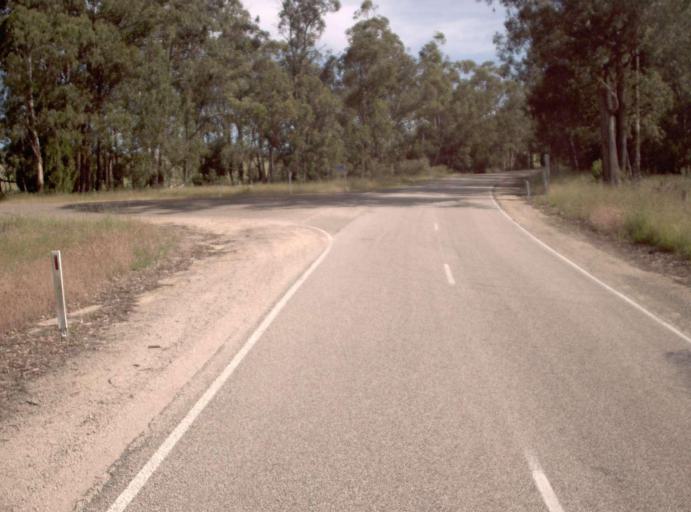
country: AU
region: Victoria
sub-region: East Gippsland
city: Lakes Entrance
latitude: -37.5372
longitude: 148.1480
